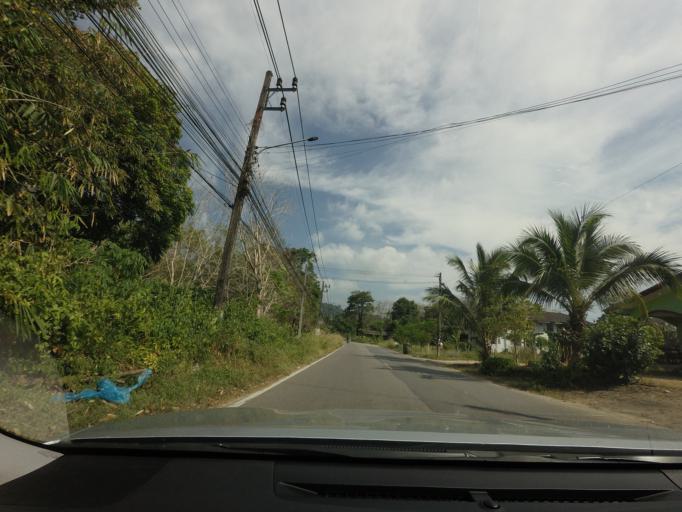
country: TH
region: Phangnga
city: Ban Khao Lak
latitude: 8.7238
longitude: 98.2539
